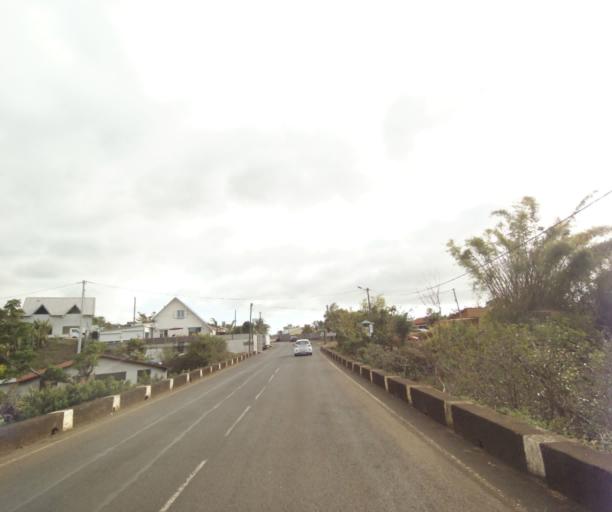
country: RE
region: Reunion
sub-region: Reunion
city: Saint-Paul
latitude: -21.0382
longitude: 55.3061
